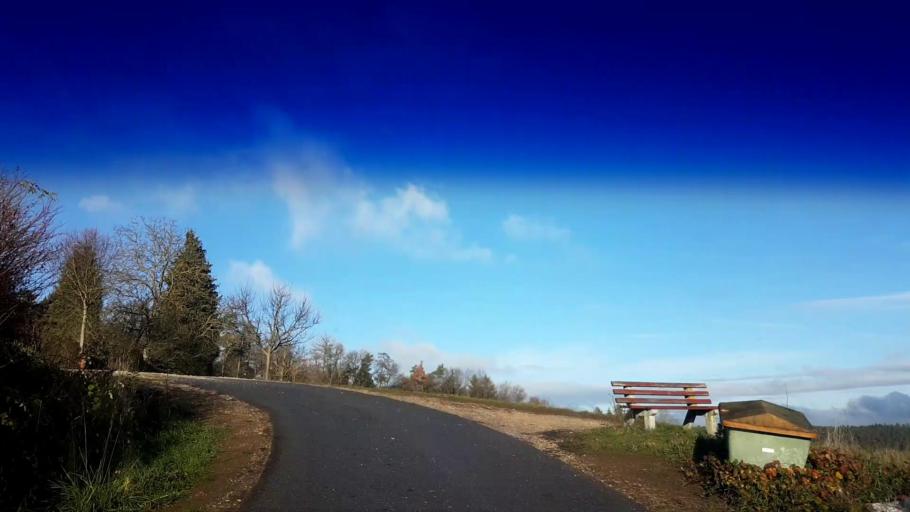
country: DE
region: Bavaria
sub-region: Upper Franconia
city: Pettstadt
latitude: 49.8375
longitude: 10.9204
